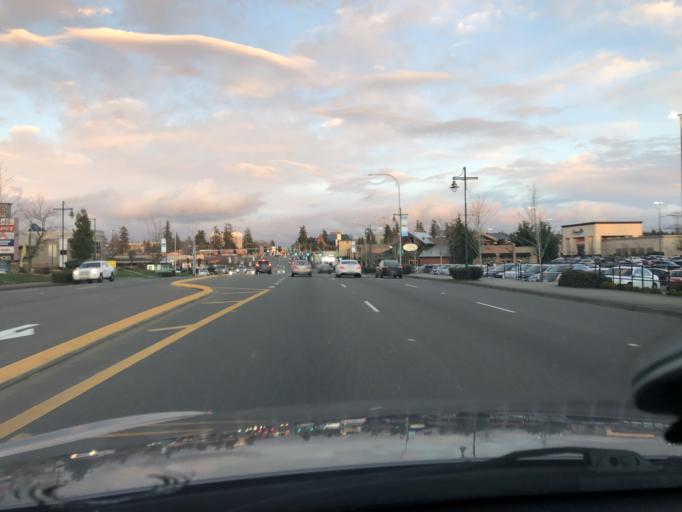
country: US
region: Washington
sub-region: King County
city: Federal Way
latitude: 47.3150
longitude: -122.3104
